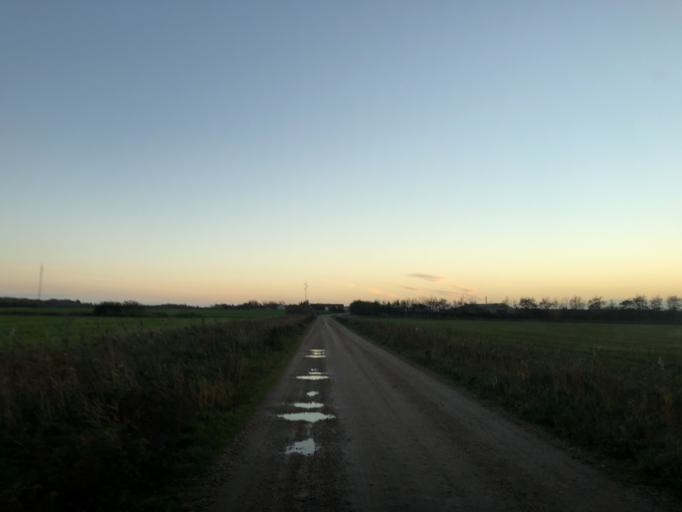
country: DK
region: Central Jutland
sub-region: Holstebro Kommune
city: Ulfborg
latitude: 56.2855
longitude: 8.2905
